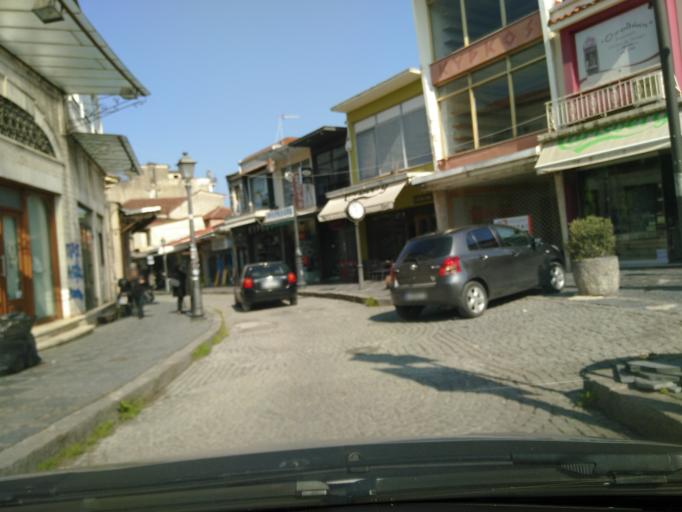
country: GR
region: Epirus
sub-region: Nomos Ioanninon
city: Ioannina
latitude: 39.6690
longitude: 20.8560
